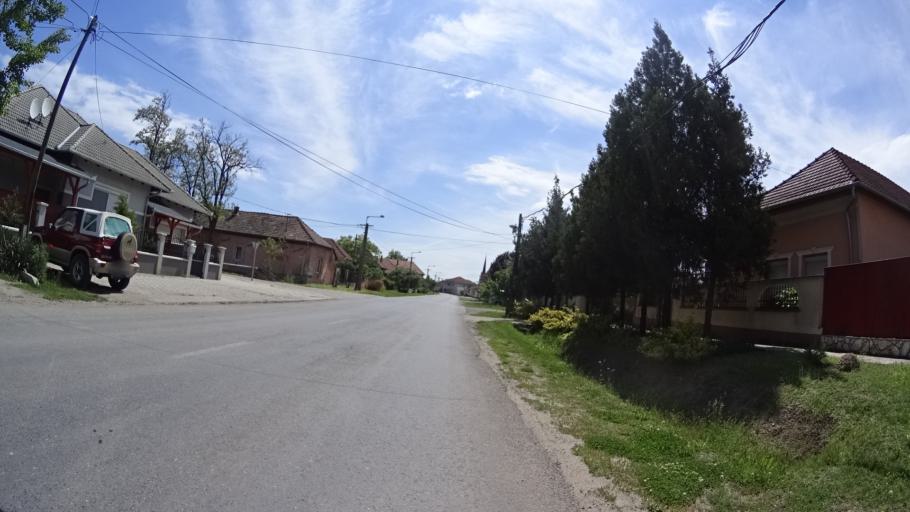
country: HU
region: Bacs-Kiskun
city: Tiszakecske
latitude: 46.9307
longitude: 20.1098
